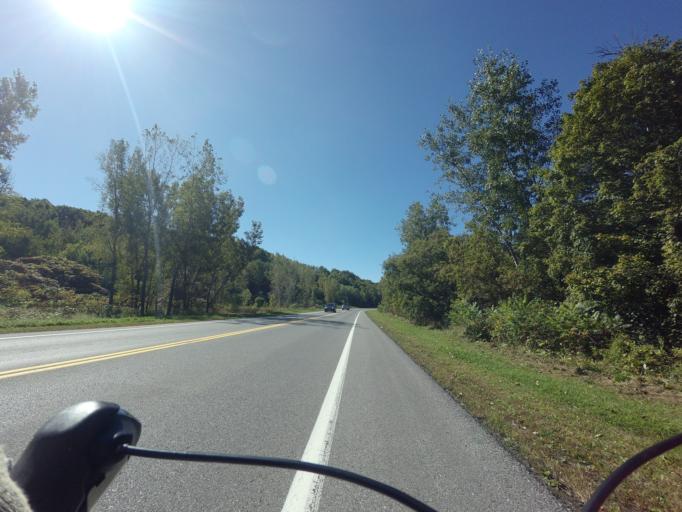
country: CA
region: Quebec
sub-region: Outaouais
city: Gatineau
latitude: 45.4603
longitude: -75.6263
